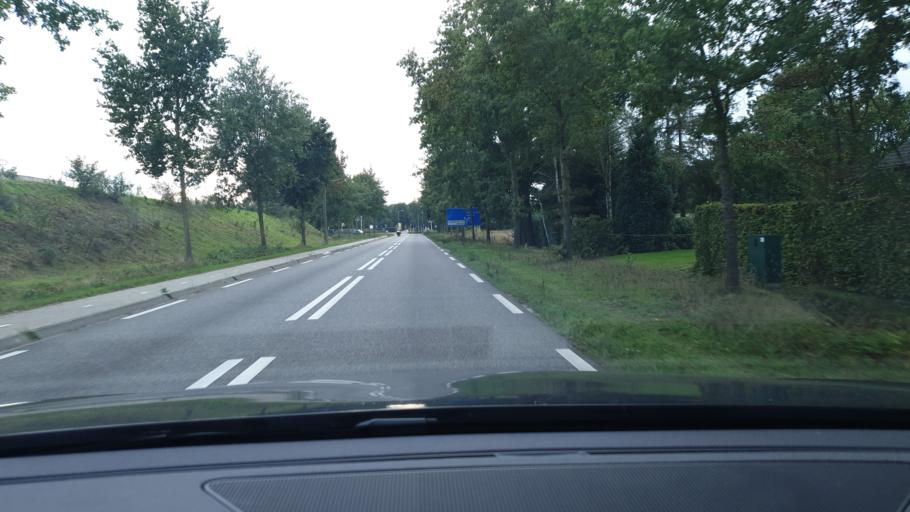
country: NL
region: Limburg
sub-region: Gemeente Peel en Maas
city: Maasbree
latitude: 51.4510
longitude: 6.0764
